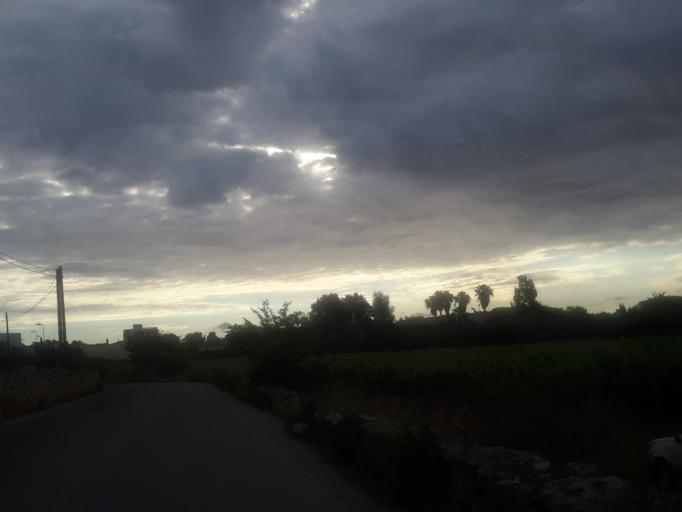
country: ES
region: Catalonia
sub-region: Provincia de Barcelona
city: Vilanova i la Geltru
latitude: 41.2419
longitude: 1.7177
